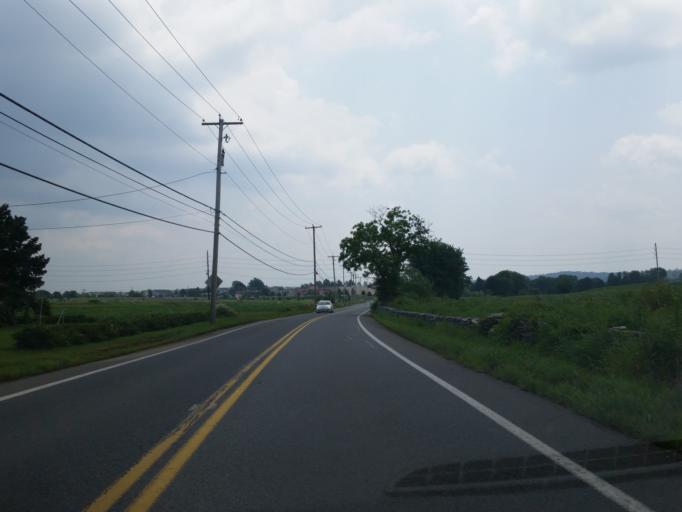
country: US
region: Pennsylvania
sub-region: Lebanon County
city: Campbelltown
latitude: 40.2861
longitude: -76.5962
